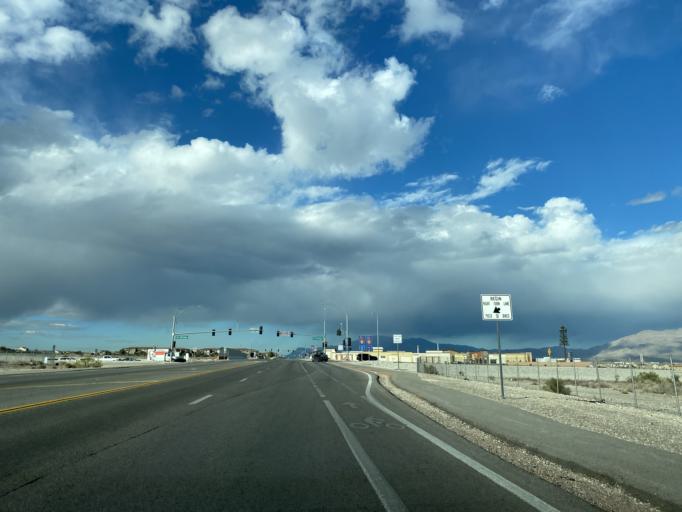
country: US
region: Nevada
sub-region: Clark County
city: Summerlin South
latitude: 36.2794
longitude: -115.3149
